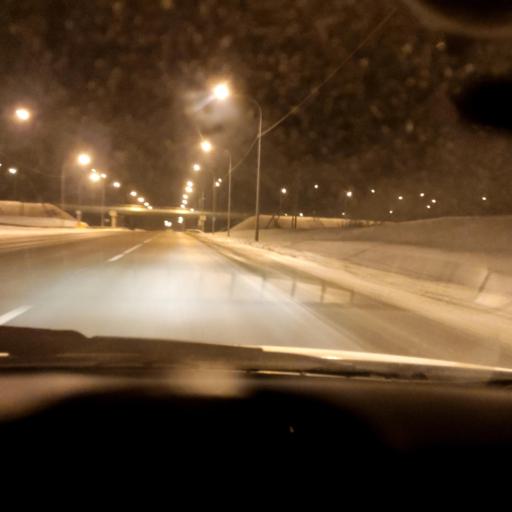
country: RU
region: Kursk
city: Fatezh
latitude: 52.0966
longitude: 35.8210
